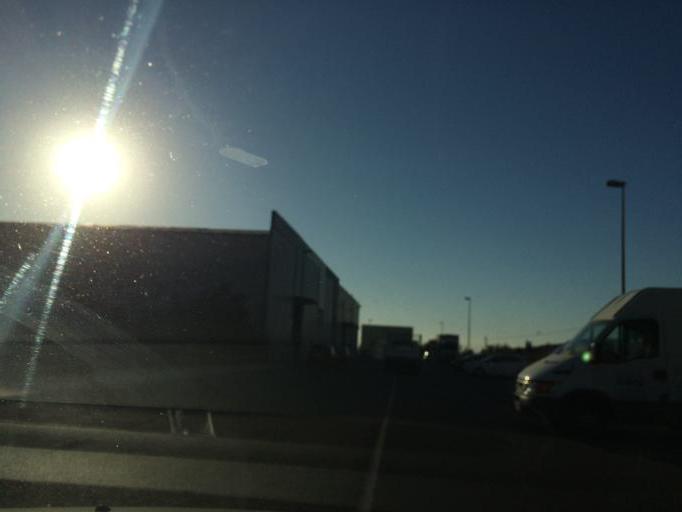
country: ES
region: Andalusia
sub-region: Provincia de Almeria
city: Viator
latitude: 36.8768
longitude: -2.4129
